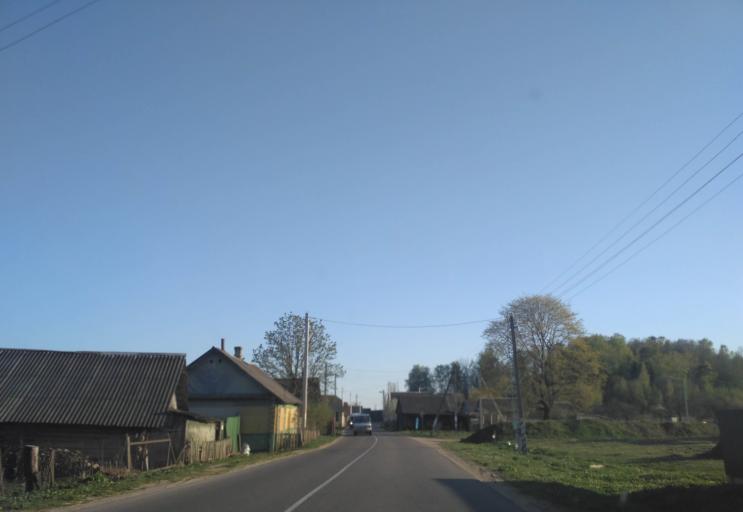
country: BY
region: Minsk
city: Radashkovichy
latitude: 54.1401
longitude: 27.2077
